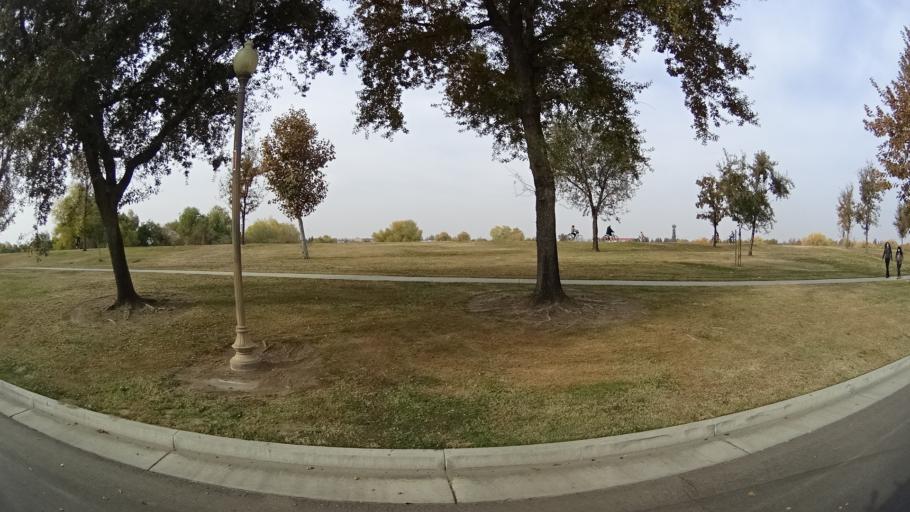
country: US
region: California
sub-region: Kern County
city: Rosedale
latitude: 35.3475
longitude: -119.1362
